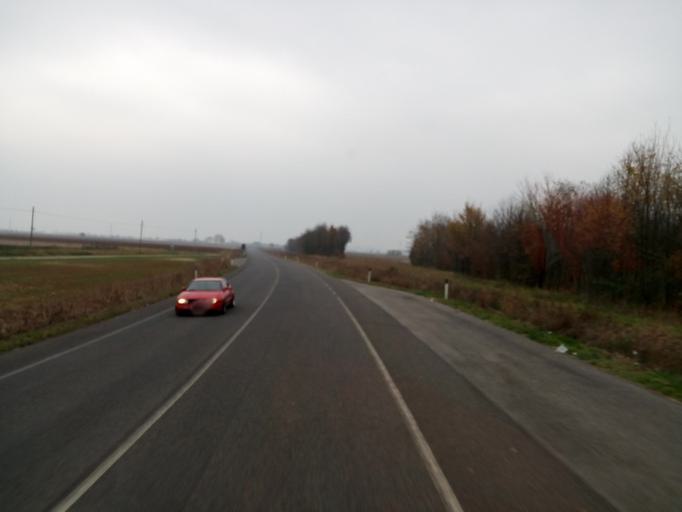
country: IT
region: Friuli Venezia Giulia
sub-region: Provincia di Udine
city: Orsaria
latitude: 46.0380
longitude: 13.3538
